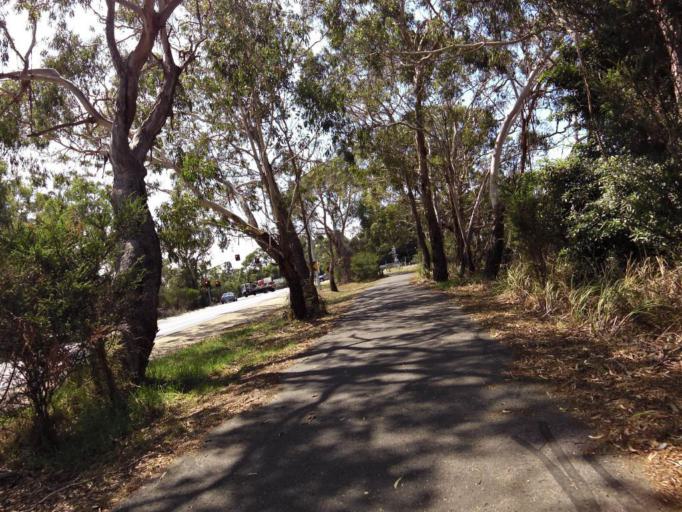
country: AU
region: Victoria
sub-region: Mornington Peninsula
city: Crib Point
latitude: -38.3300
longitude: 145.1827
